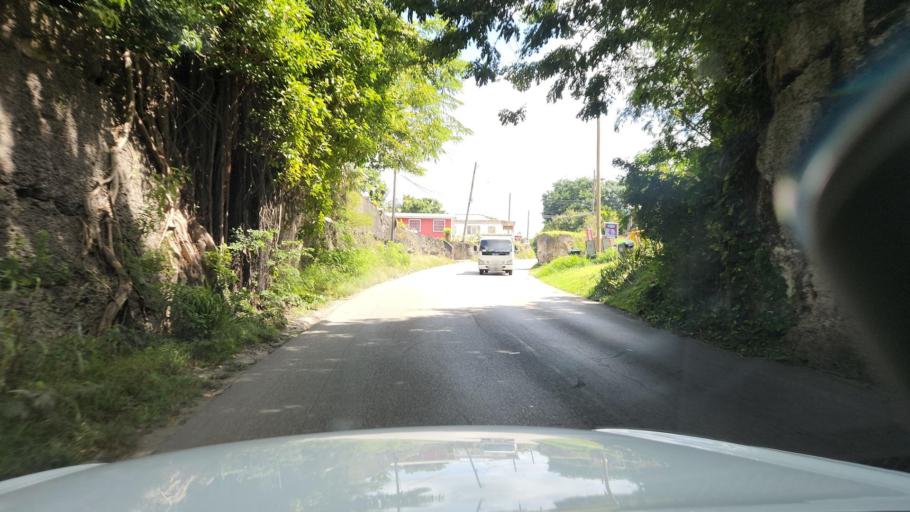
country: BB
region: Saint Michael
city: Bridgetown
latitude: 13.1066
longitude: -59.5736
